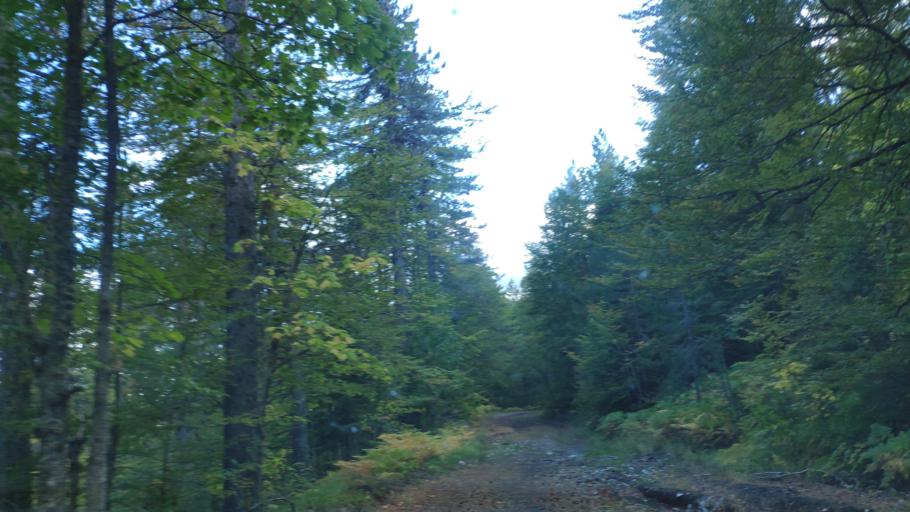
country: AL
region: Korce
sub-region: Rrethi i Devollit
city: Miras
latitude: 40.3472
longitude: 20.8990
